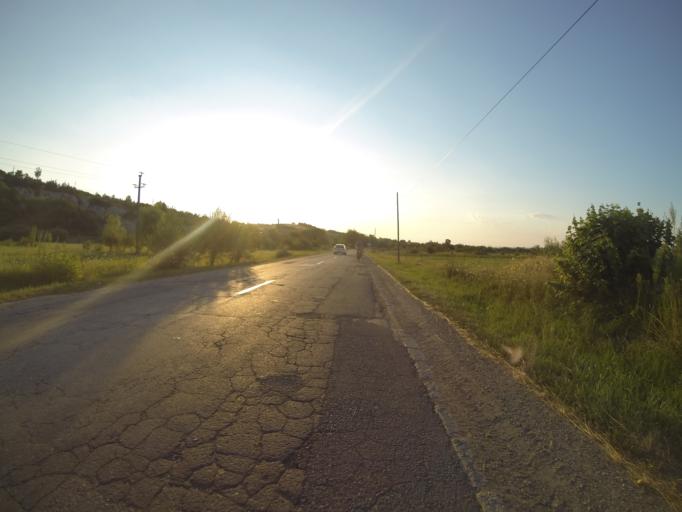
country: RO
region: Brasov
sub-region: Comuna Sinca Veche
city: Sinca Veche
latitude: 45.7512
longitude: 25.1815
